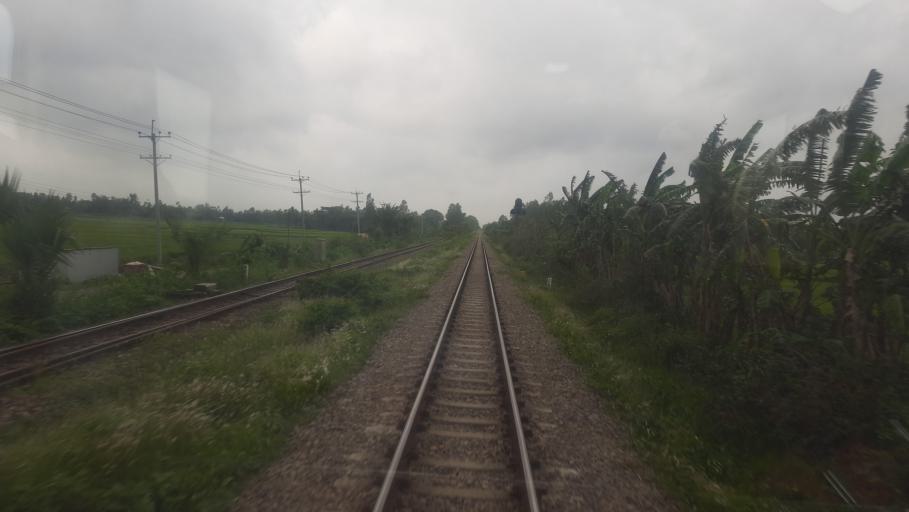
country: BD
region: Dhaka
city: Narsingdi
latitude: 23.9506
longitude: 90.7947
